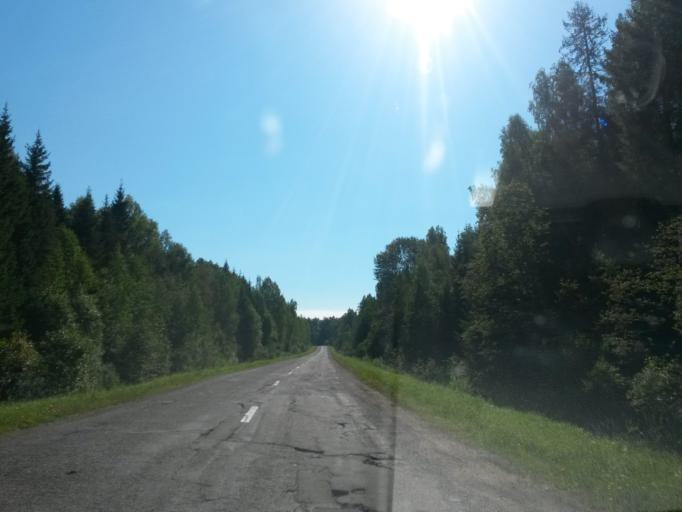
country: RU
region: Jaroslavl
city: Dubki
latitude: 57.2942
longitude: 40.0927
